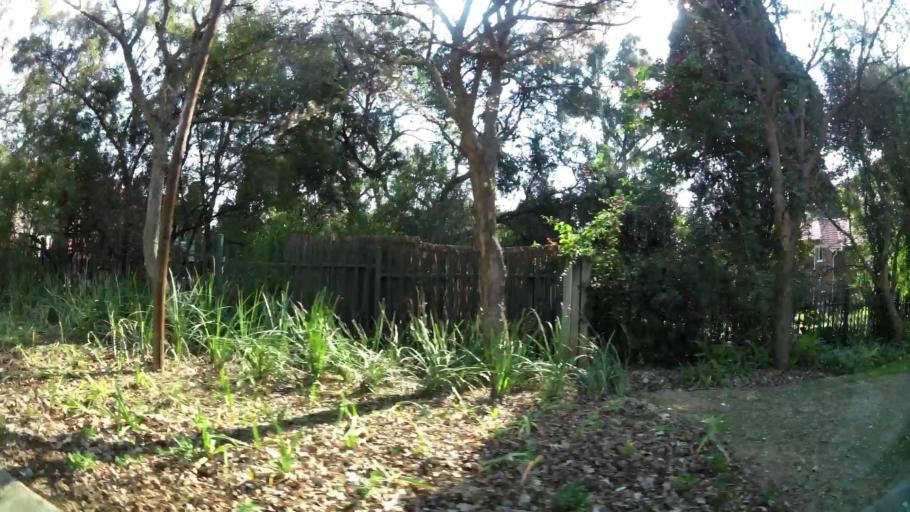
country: ZA
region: Gauteng
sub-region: City of Johannesburg Metropolitan Municipality
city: Modderfontein
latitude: -26.1056
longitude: 28.1535
